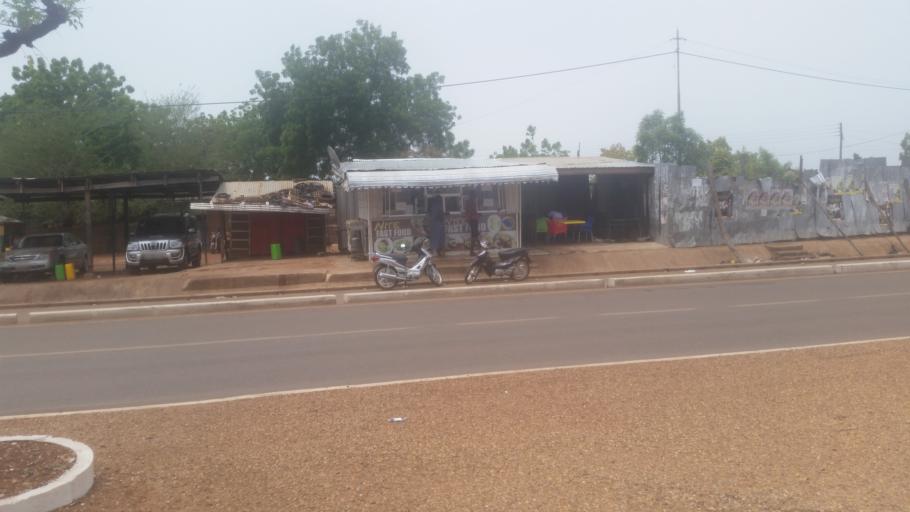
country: GH
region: Northern
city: Tamale
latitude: 9.3965
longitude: -0.8269
